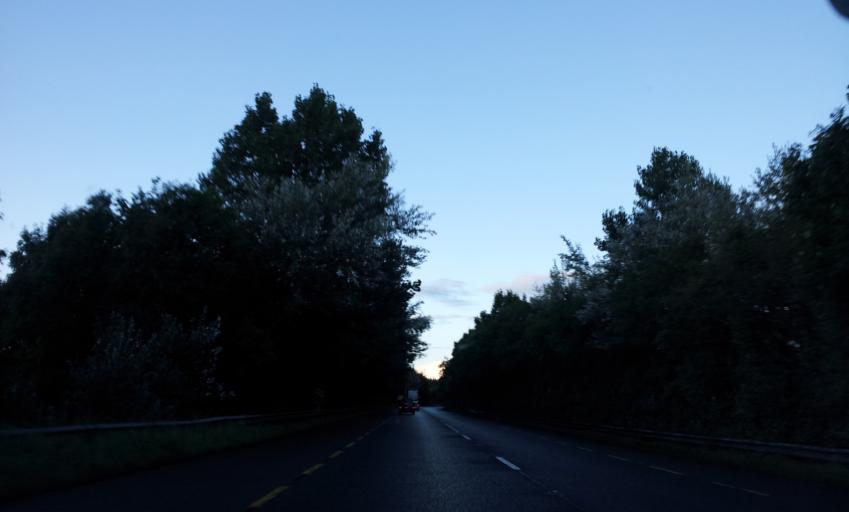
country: IE
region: Munster
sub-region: County Limerick
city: Rathkeale
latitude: 52.5230
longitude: -8.9471
